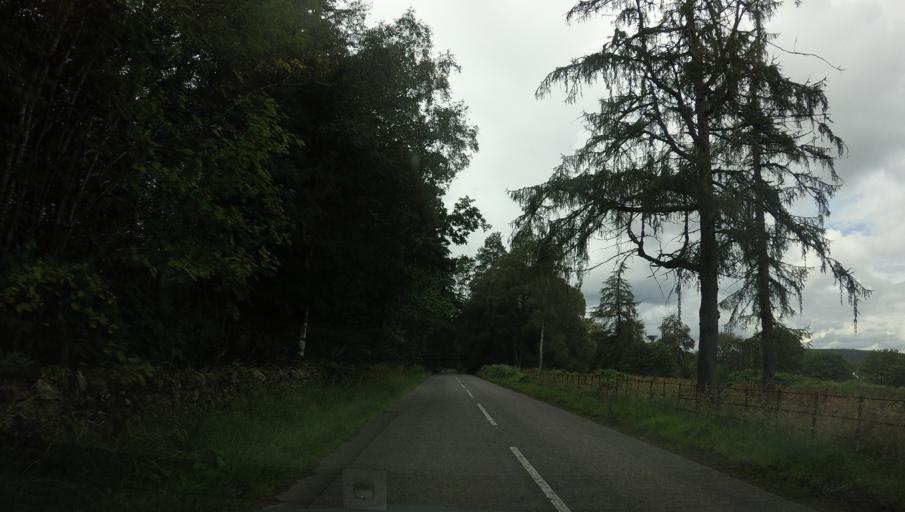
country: GB
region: Scotland
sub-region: Aberdeenshire
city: Aboyne
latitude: 57.0702
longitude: -2.7711
